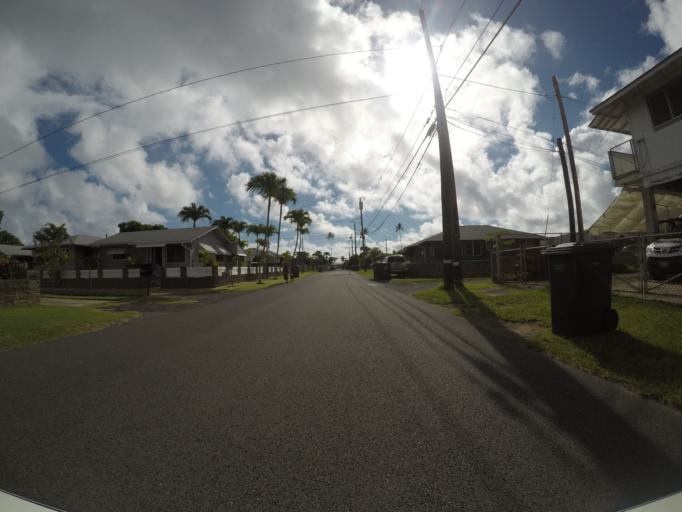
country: US
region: Hawaii
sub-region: Honolulu County
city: Kailua
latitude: 21.4010
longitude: -157.7457
